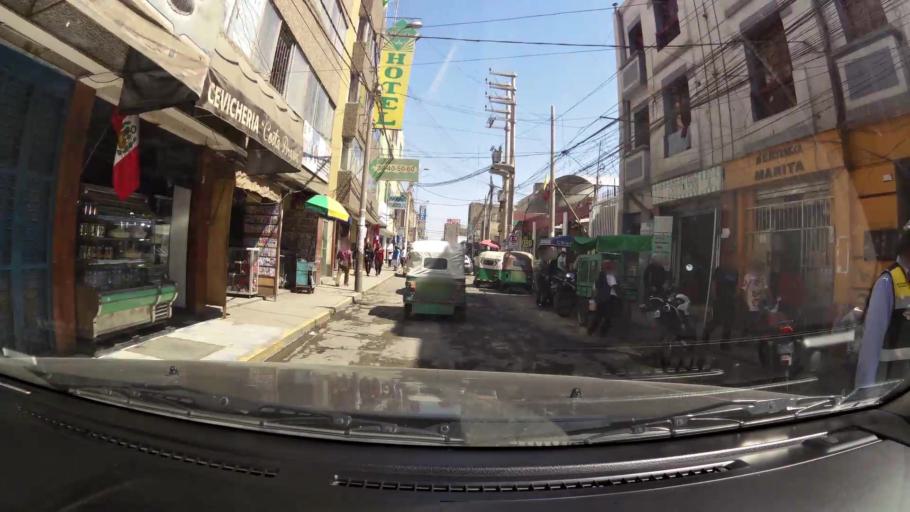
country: PE
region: Ica
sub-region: Provincia de Ica
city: Ica
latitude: -14.0621
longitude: -75.7283
